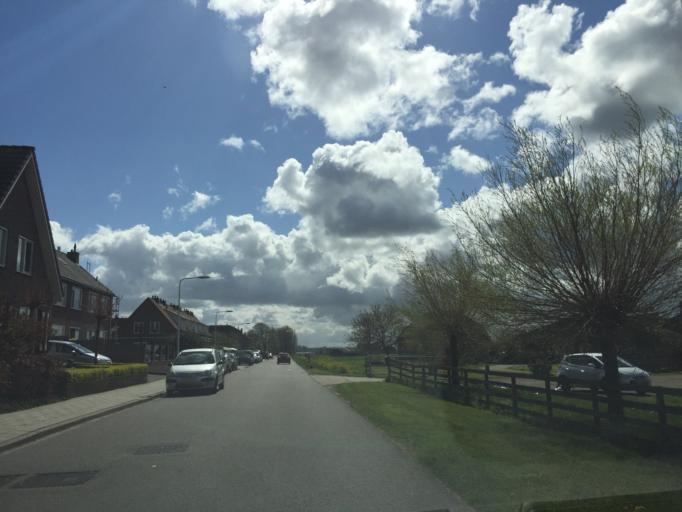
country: NL
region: South Holland
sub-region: Gemeente Kaag en Braassem
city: Oude Wetering
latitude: 52.2036
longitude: 4.6143
